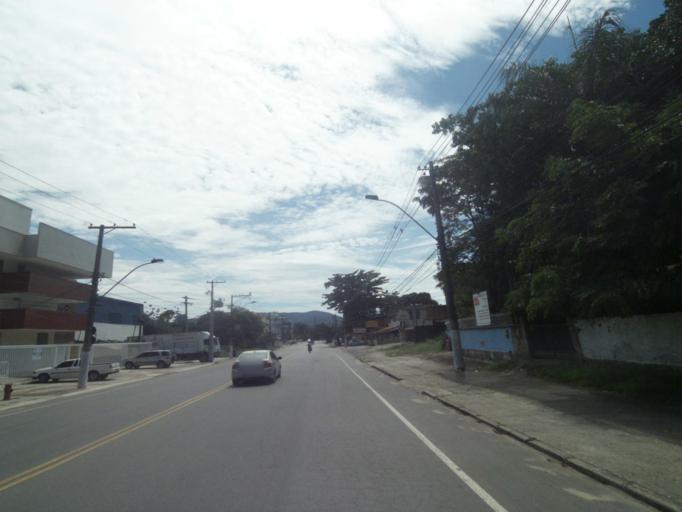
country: BR
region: Rio de Janeiro
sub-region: Niteroi
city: Niteroi
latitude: -22.9618
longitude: -43.0302
